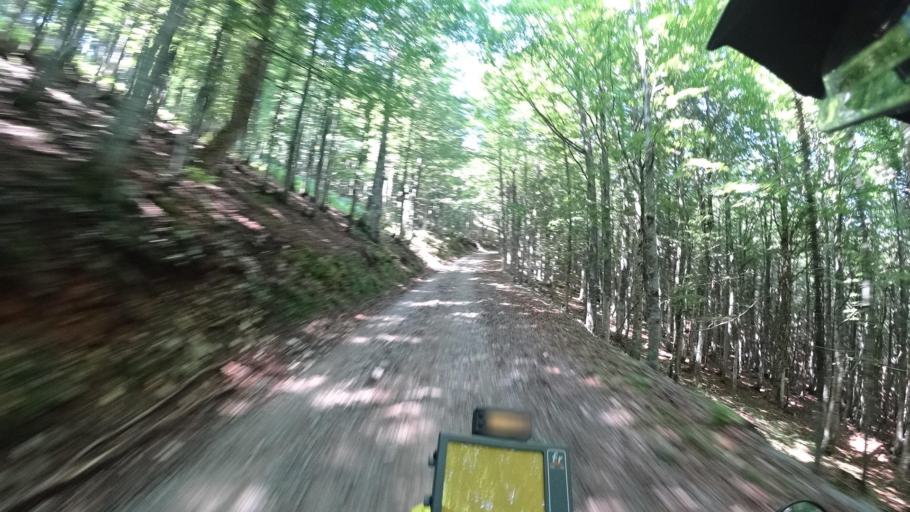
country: HR
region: Primorsko-Goranska
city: Vrbovsko
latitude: 45.2703
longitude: 14.9340
